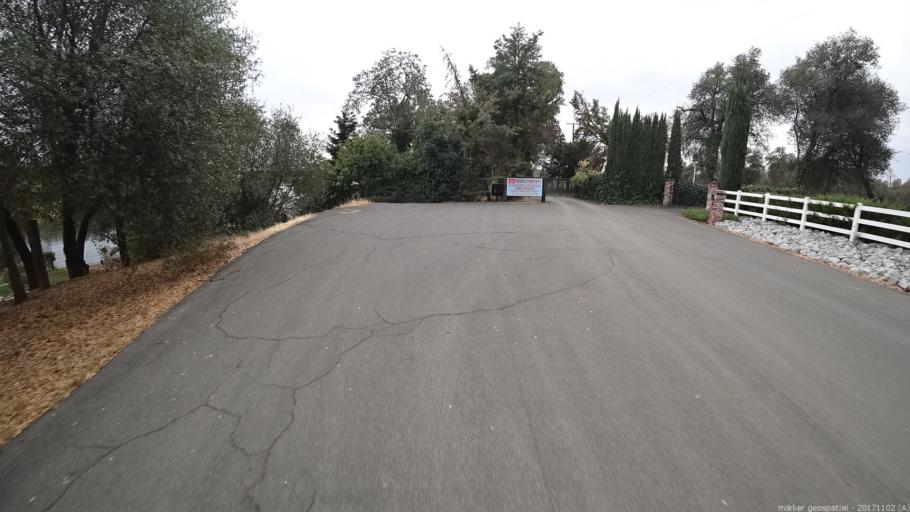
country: US
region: California
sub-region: Shasta County
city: Shasta Lake
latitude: 40.6513
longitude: -122.3166
